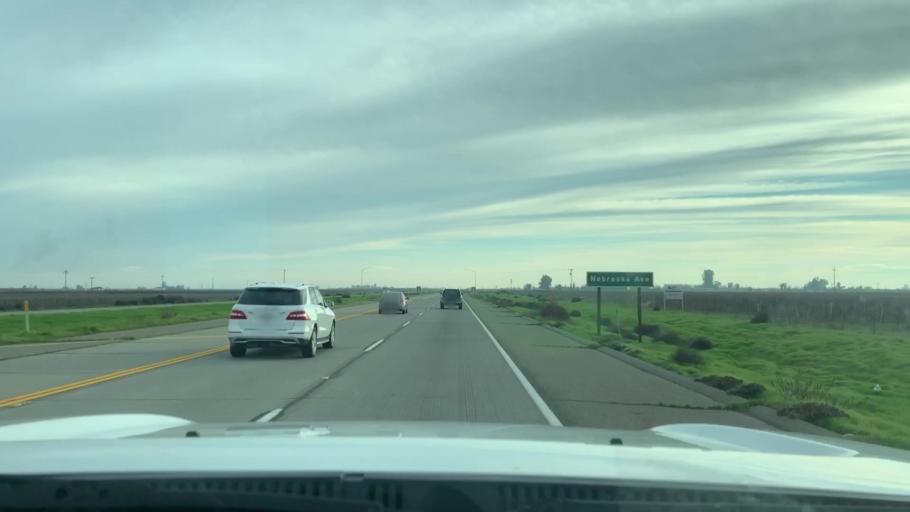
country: US
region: California
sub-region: Fresno County
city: Caruthers
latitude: 36.5651
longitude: -119.7863
